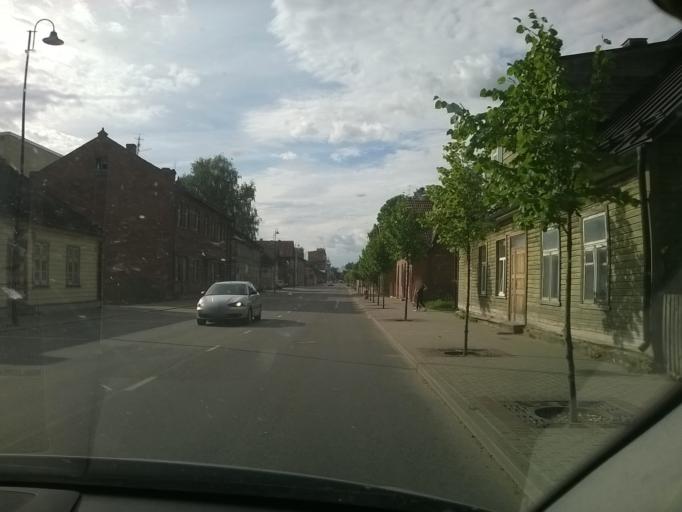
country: EE
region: Vorumaa
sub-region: Voru linn
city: Voru
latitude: 57.8419
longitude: 27.0011
